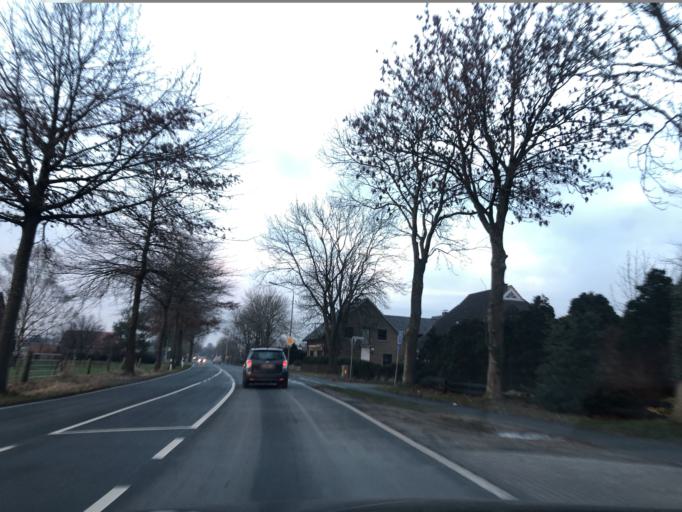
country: DE
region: Lower Saxony
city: Lemwerder
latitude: 53.1510
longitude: 8.6080
